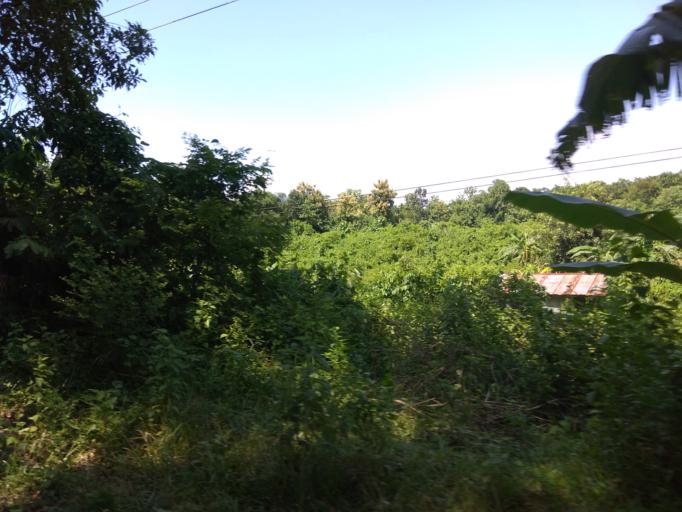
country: BD
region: Chittagong
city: Khagrachhari
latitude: 23.0289
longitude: 92.0142
